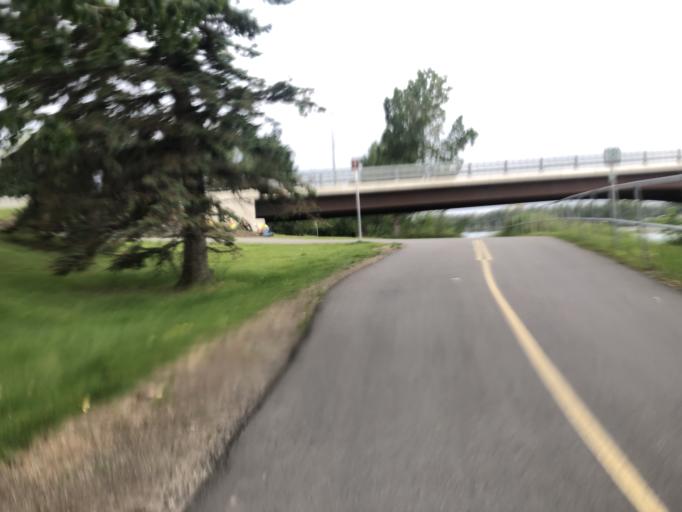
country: CA
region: Alberta
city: Calgary
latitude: 51.0426
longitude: -114.0322
